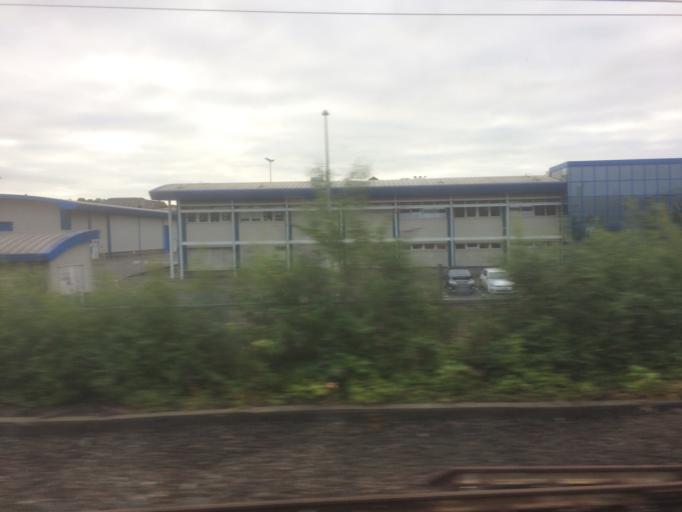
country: GB
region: Scotland
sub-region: Glasgow City
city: Glasgow
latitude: 55.8831
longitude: -4.2387
